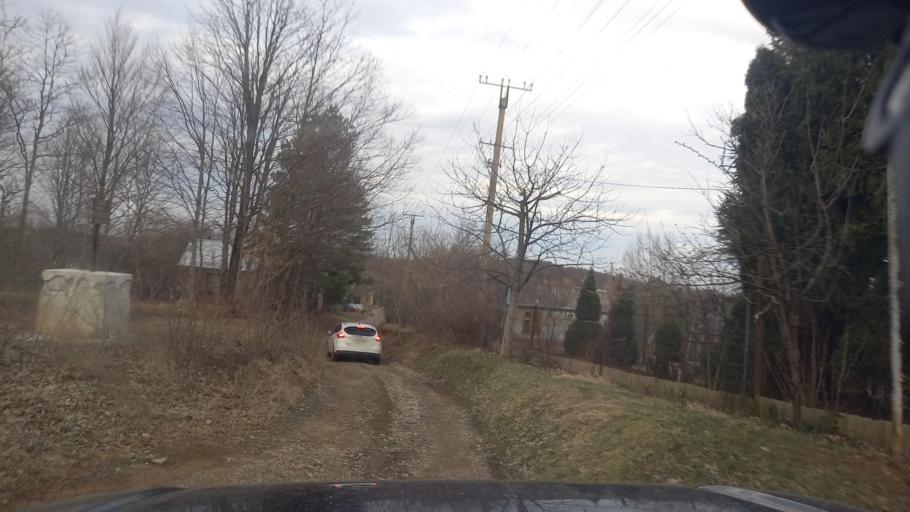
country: RU
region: Krasnodarskiy
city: Goryachiy Klyuch
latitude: 44.6935
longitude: 39.0166
